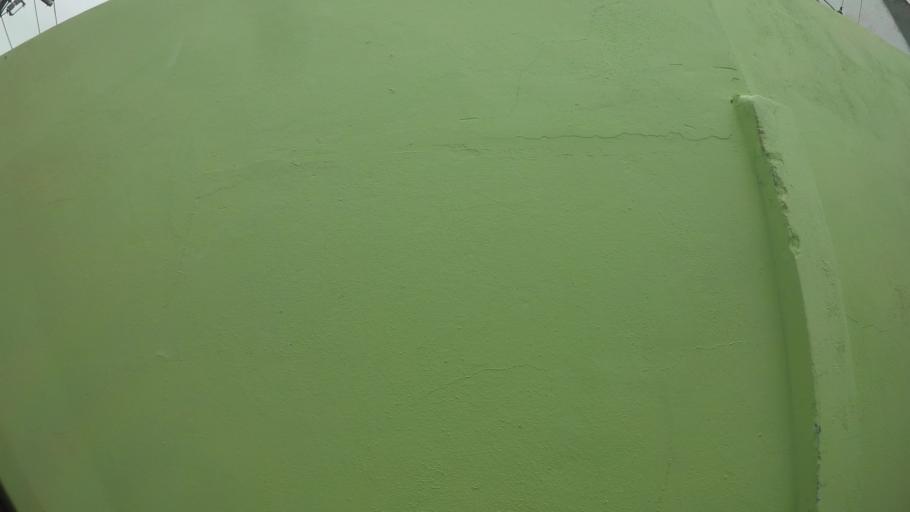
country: TH
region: Rayong
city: Rayong
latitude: 12.6634
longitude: 101.2710
